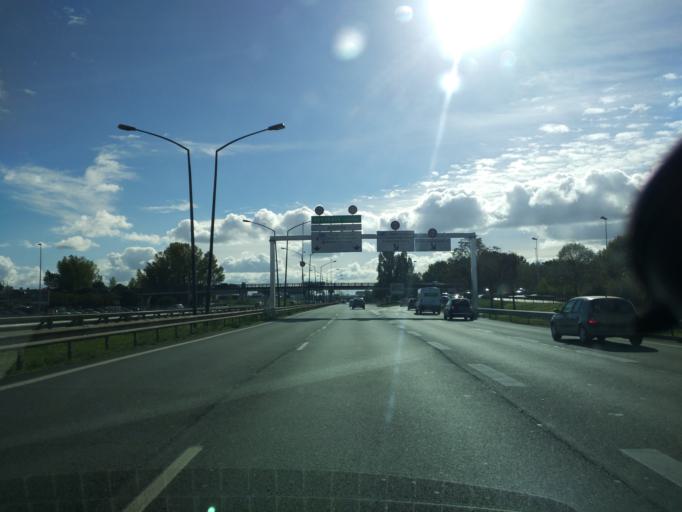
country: FR
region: Aquitaine
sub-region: Departement de la Gironde
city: Le Bouscat
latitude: 44.8793
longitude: -0.5632
